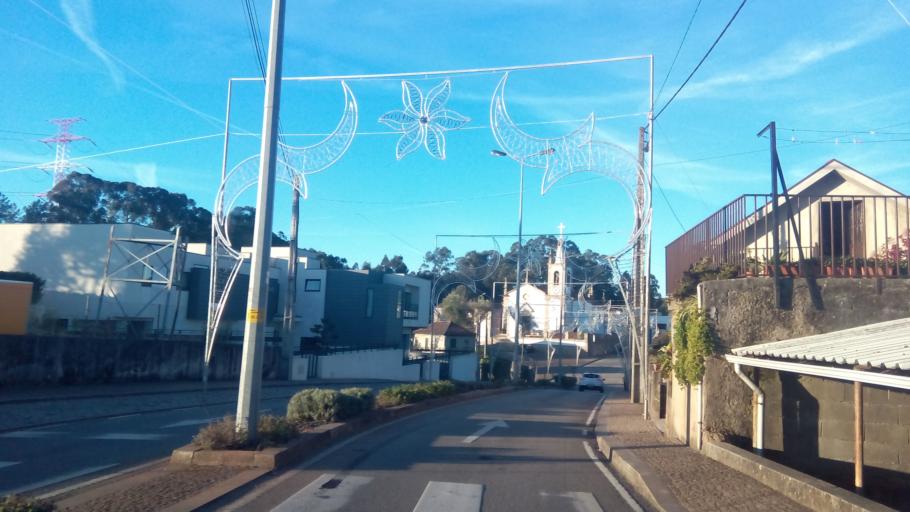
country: PT
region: Porto
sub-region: Paredes
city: Baltar
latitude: 41.1846
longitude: -8.3765
